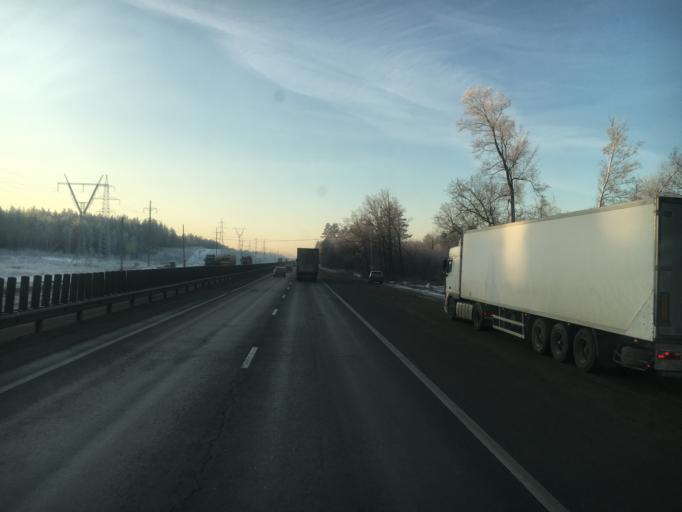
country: RU
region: Samara
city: Pribrezhnyy
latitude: 53.5139
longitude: 49.9015
